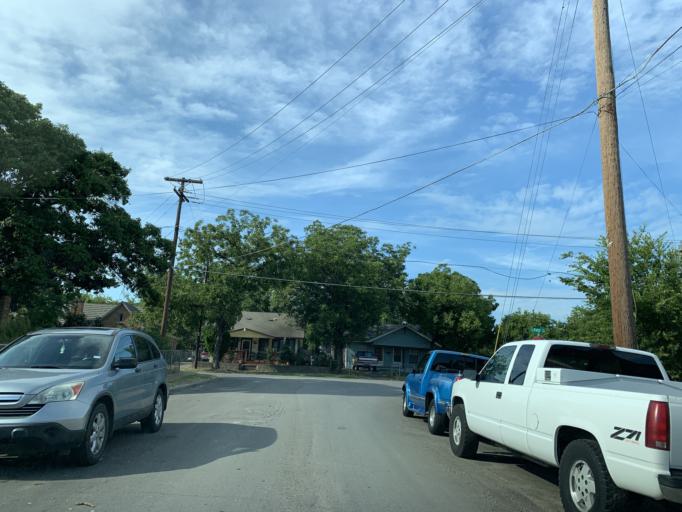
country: US
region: Texas
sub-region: Dallas County
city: Cockrell Hill
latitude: 32.7399
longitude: -96.8361
